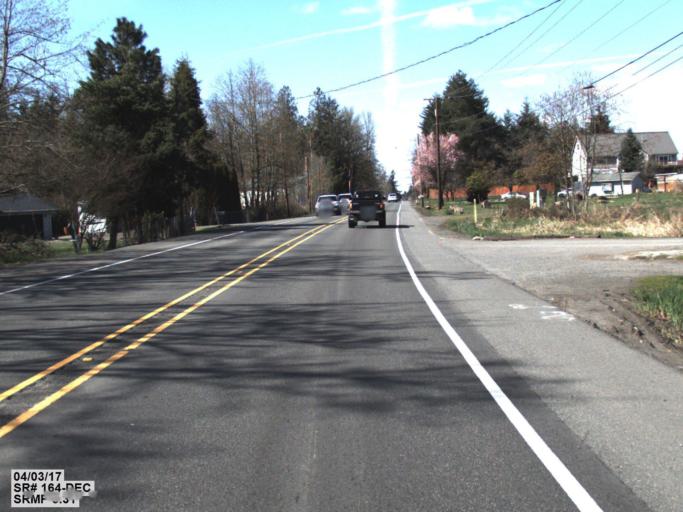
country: US
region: Washington
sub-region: King County
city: Lea Hill
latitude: 47.2646
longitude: -122.1424
